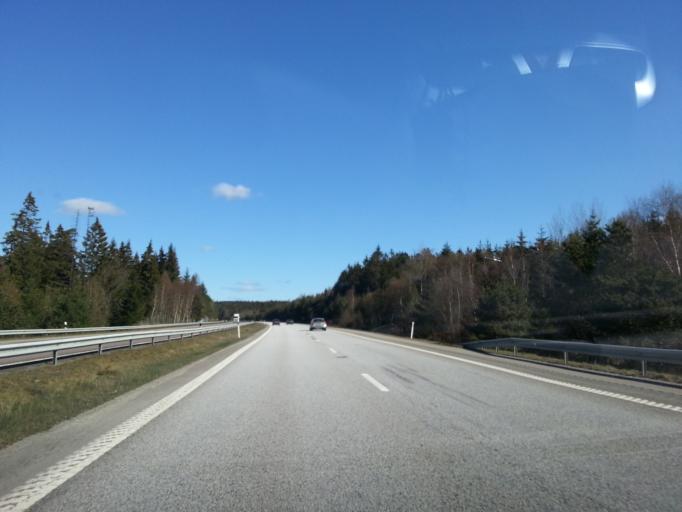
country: SE
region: Vaestra Goetaland
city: Svanesund
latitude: 58.1265
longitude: 11.8843
